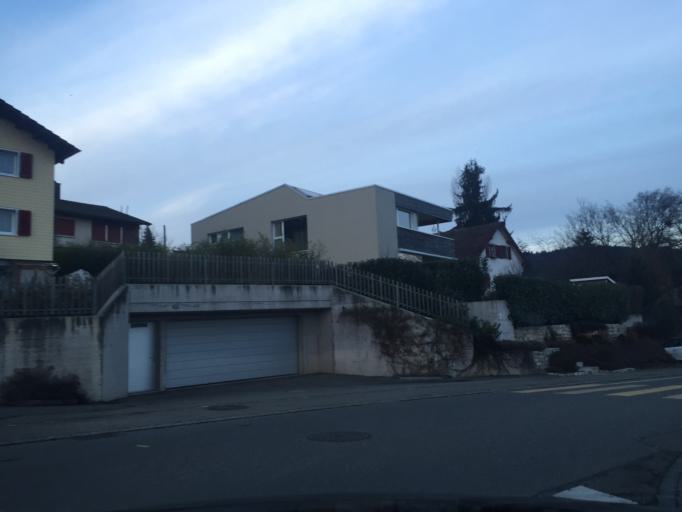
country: CH
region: Thurgau
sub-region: Frauenfeld District
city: Diessenhofen
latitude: 47.6876
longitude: 8.7443
